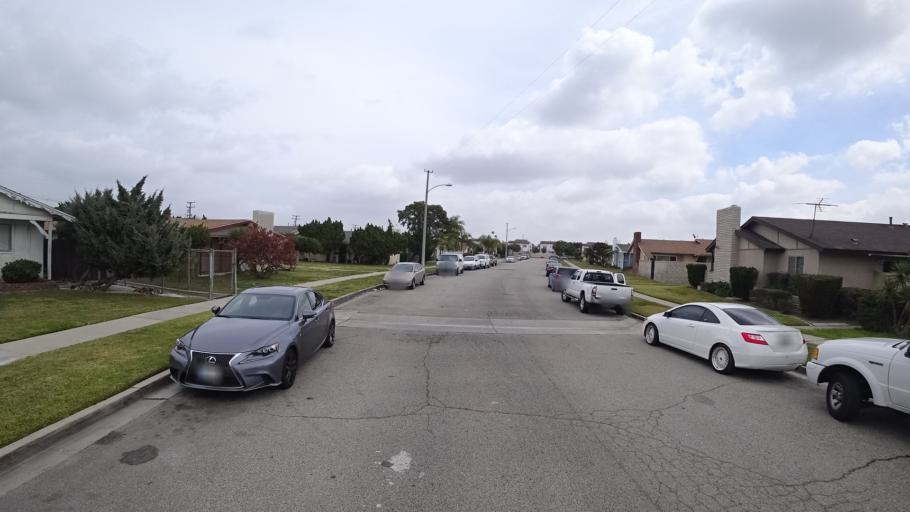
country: US
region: California
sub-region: Orange County
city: Buena Park
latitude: 33.8350
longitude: -117.9976
